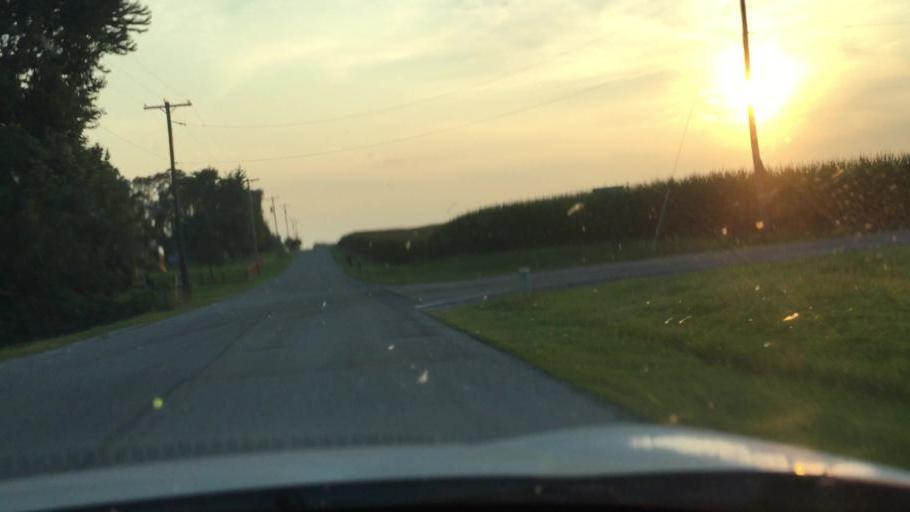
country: US
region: Ohio
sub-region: Madison County
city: Choctaw Lake
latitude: 39.9484
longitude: -83.5730
